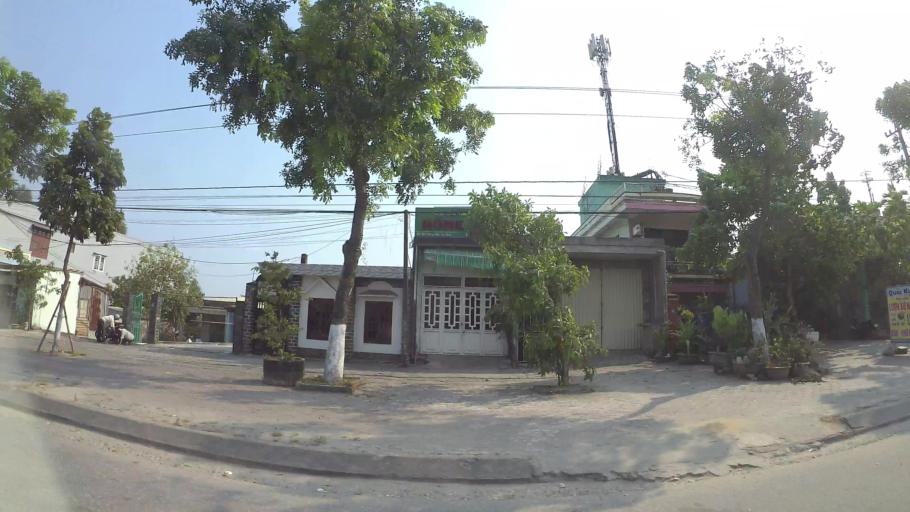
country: VN
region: Da Nang
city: Cam Le
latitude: 16.0126
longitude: 108.1818
